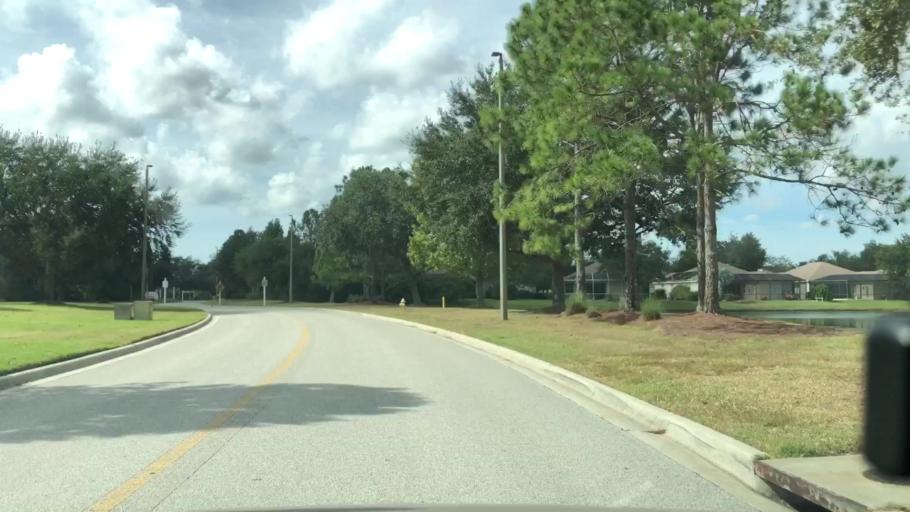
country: US
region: Florida
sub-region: Sarasota County
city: The Meadows
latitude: 27.4258
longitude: -82.4024
